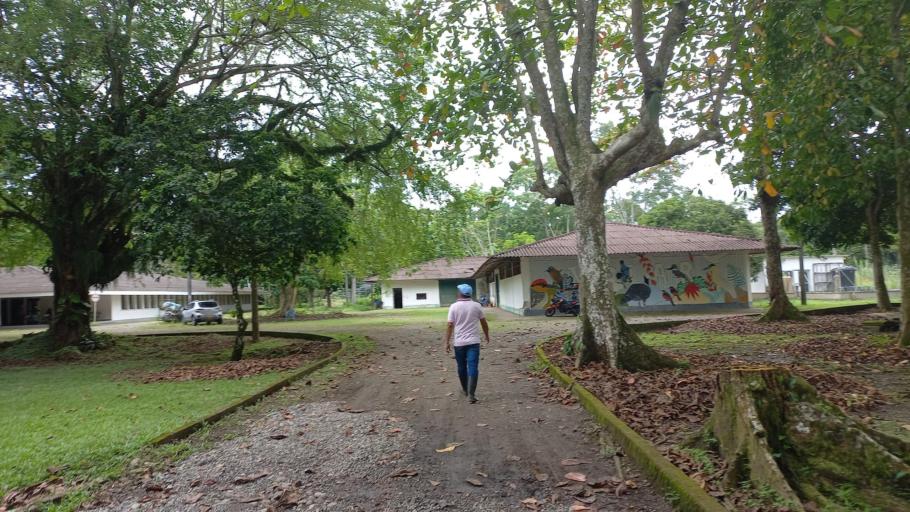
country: CO
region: Antioquia
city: Carepa
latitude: 7.7738
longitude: -76.6646
